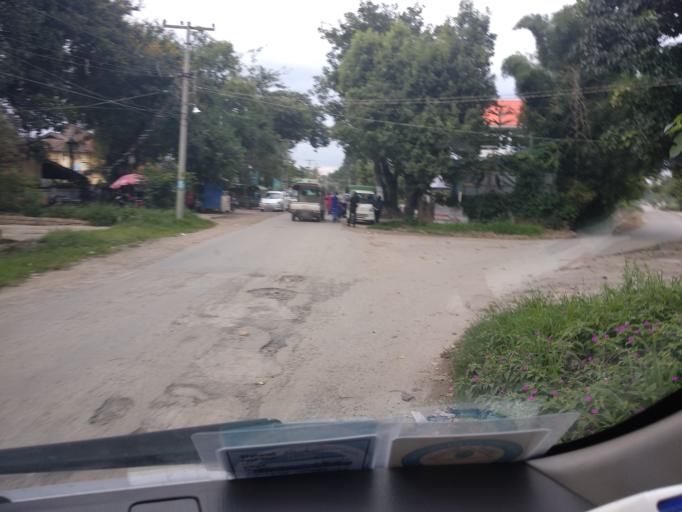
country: MM
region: Mandalay
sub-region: Pyin Oo Lwin District
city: Pyin Oo Lwin
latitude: 22.0327
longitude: 96.4777
